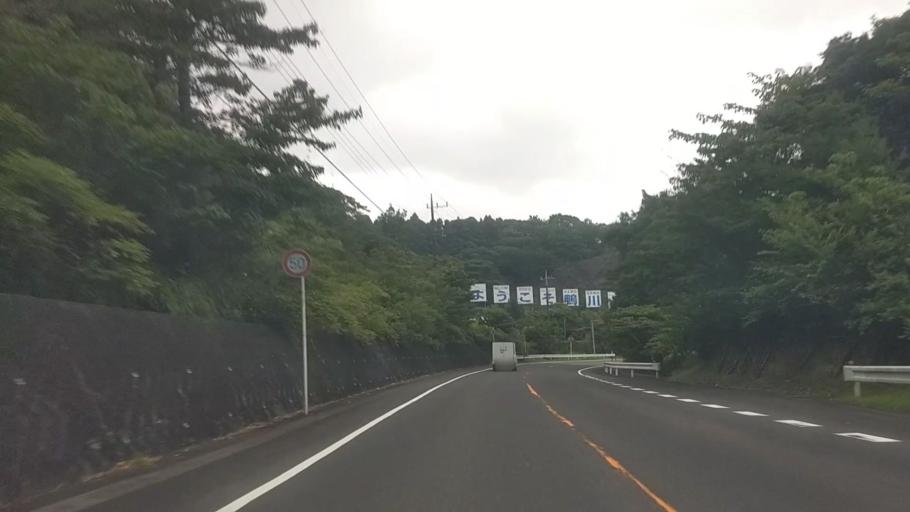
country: JP
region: Chiba
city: Kawaguchi
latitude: 35.1656
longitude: 140.0614
